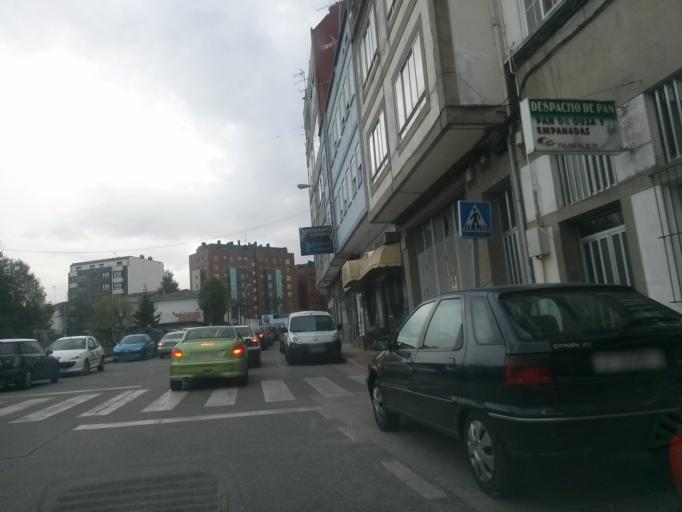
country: ES
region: Galicia
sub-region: Provincia de Lugo
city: Lugo
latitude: 43.0231
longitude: -7.5636
